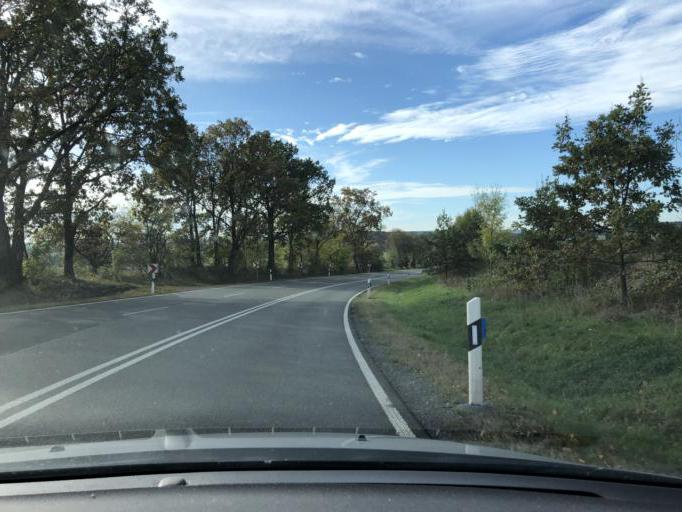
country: DE
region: Thuringia
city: Renthendorf
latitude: 50.7881
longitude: 11.9693
